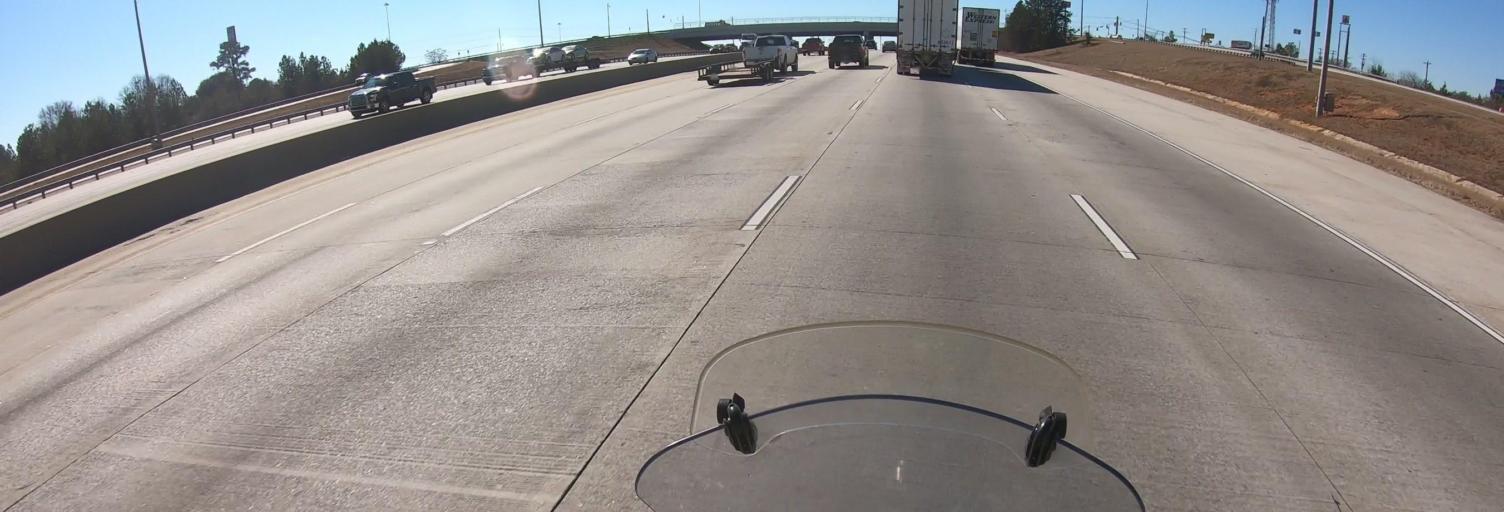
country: US
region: Georgia
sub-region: Bibb County
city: West Point
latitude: 32.7476
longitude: -83.7149
